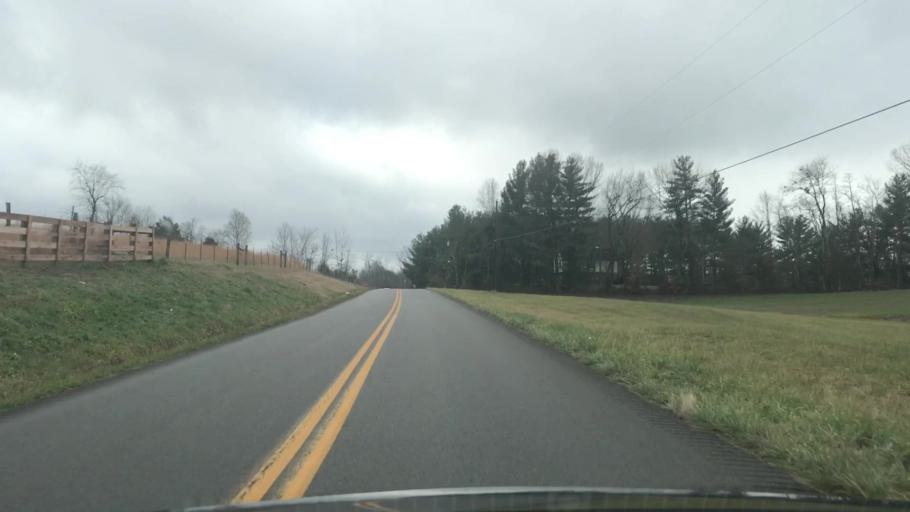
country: US
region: Kentucky
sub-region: Monroe County
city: Tompkinsville
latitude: 36.7230
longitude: -85.7095
